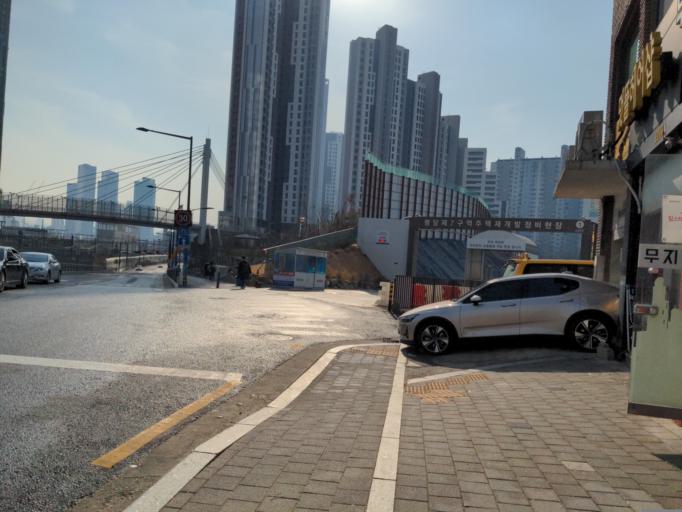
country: KR
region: Seoul
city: Seoul
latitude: 37.5581
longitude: 127.0389
